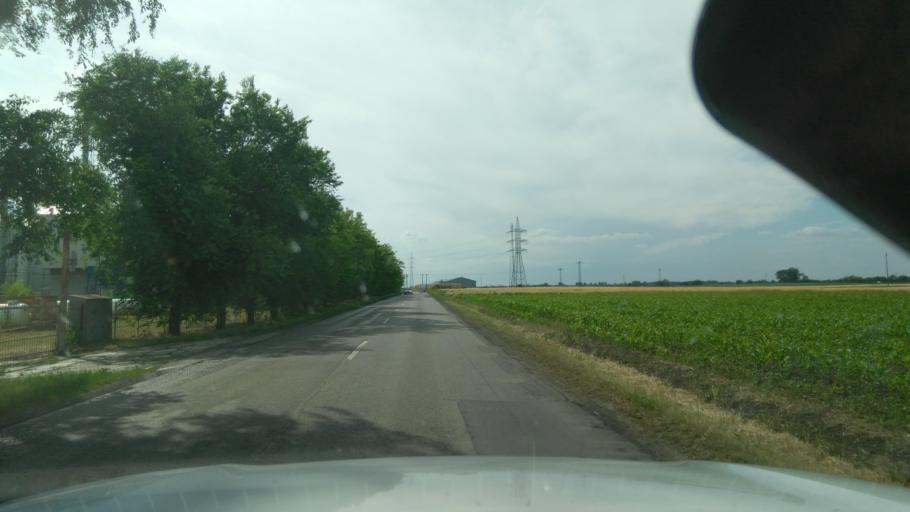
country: HU
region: Bekes
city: Medgyesegyhaza
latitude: 46.5041
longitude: 21.0147
